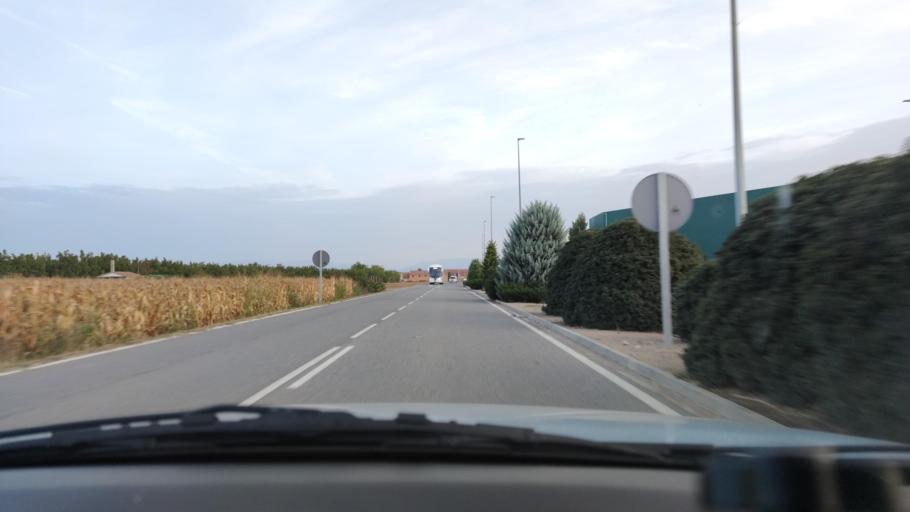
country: ES
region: Catalonia
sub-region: Provincia de Lleida
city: Mollerussa
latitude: 41.6432
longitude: 0.8763
